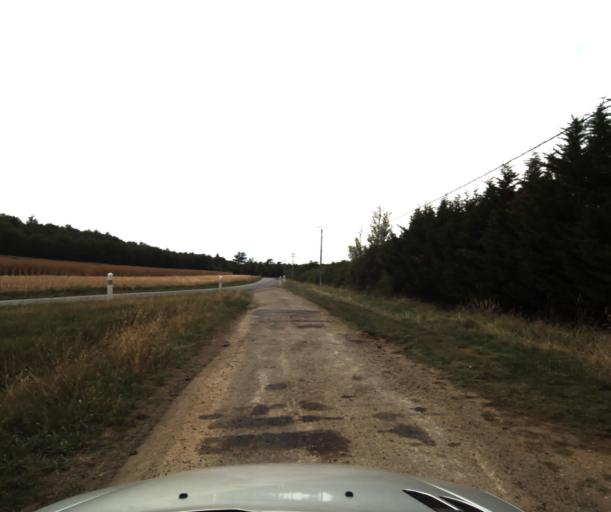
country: FR
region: Midi-Pyrenees
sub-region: Departement de la Haute-Garonne
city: Labastidette
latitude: 43.4853
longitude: 1.2166
